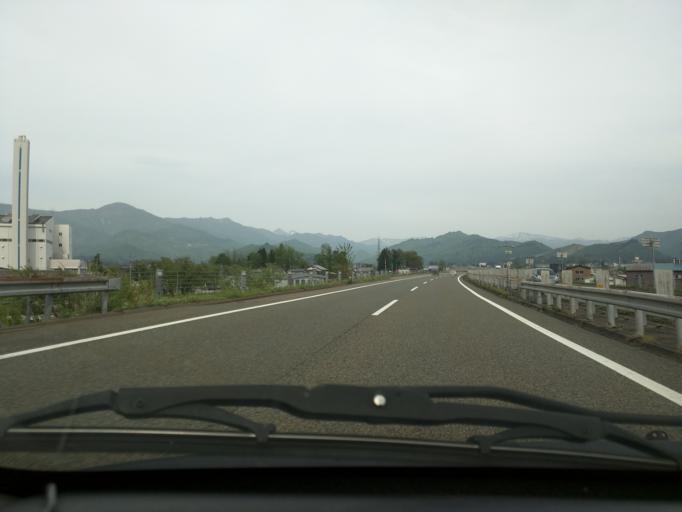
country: JP
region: Niigata
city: Ojiya
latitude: 37.2436
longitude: 138.9584
